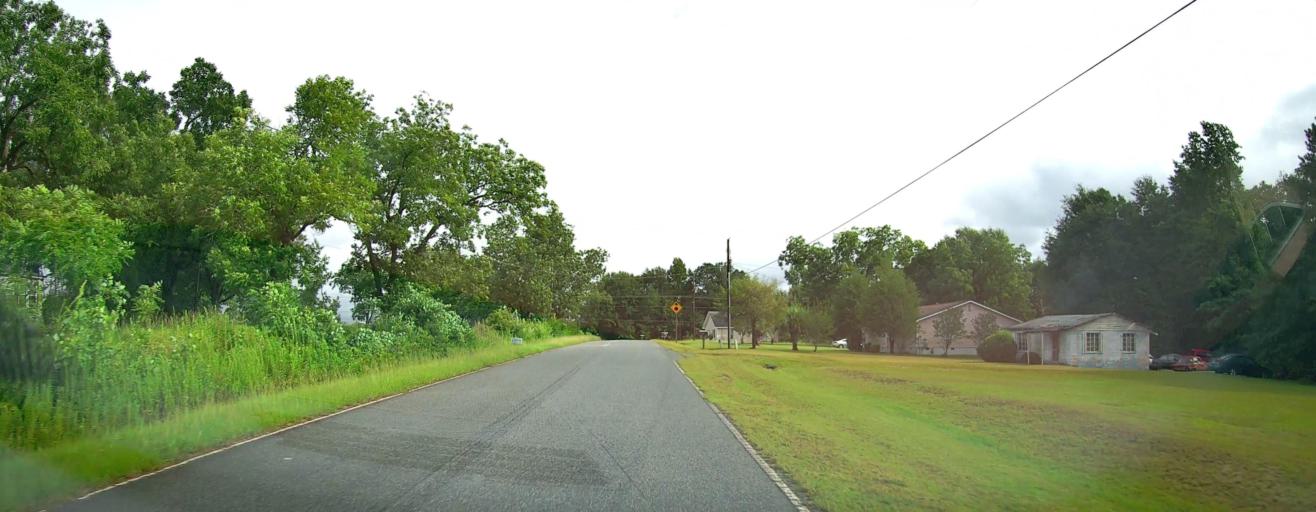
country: US
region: Georgia
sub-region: Bibb County
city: West Point
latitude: 32.8064
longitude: -83.7839
